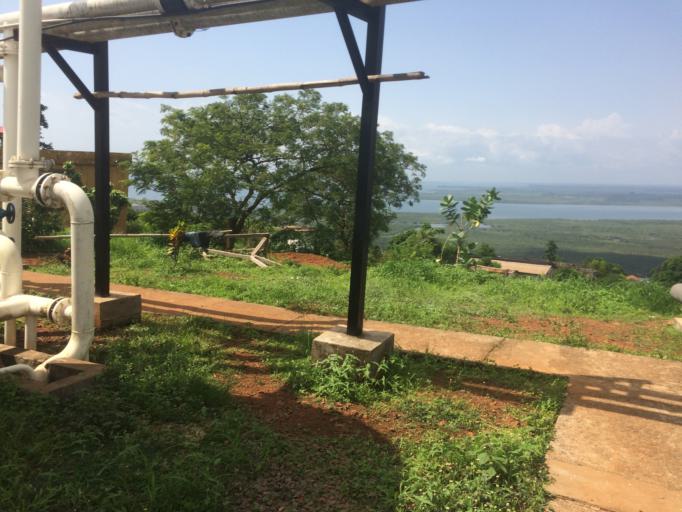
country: SL
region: Western Area
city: Hastings
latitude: 8.4105
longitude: -13.1566
